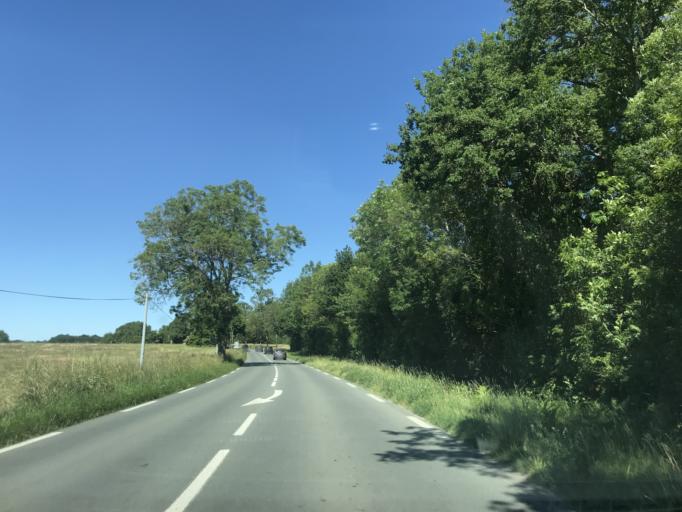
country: FR
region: Poitou-Charentes
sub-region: Departement de la Charente-Maritime
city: Cozes
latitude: 45.5774
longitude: -0.7737
